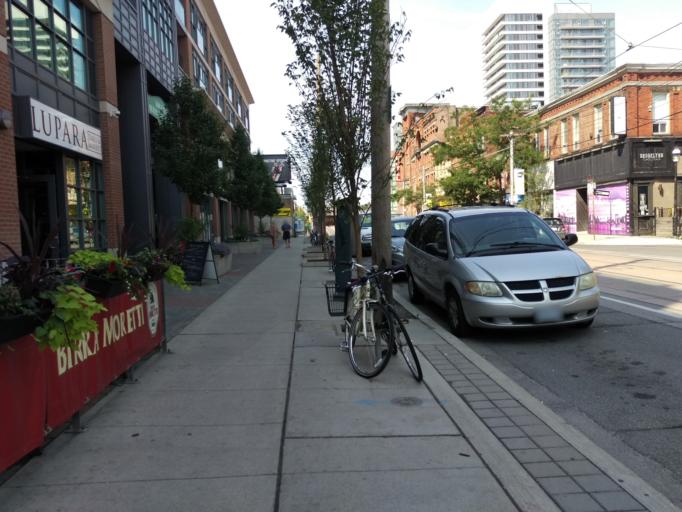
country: CA
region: Ontario
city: Toronto
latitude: 43.6428
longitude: -79.4256
